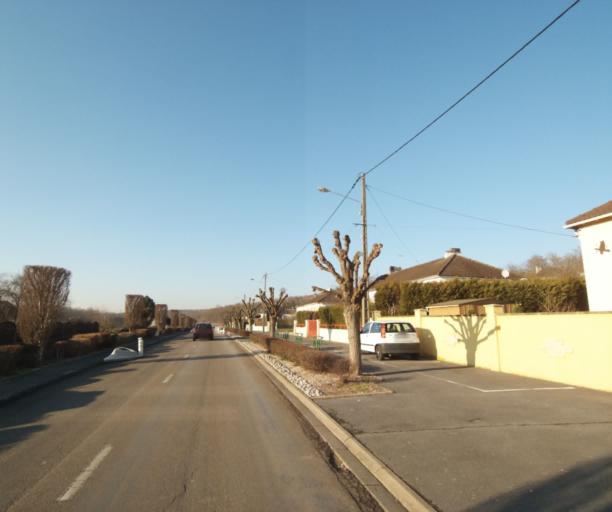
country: FR
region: Champagne-Ardenne
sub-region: Departement de la Haute-Marne
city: Bienville
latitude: 48.5573
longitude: 5.0729
